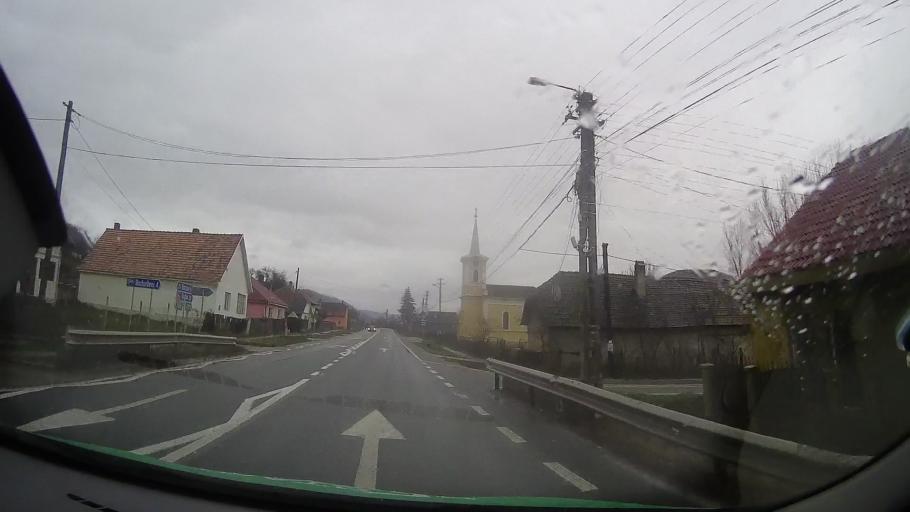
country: RO
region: Bistrita-Nasaud
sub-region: Comuna Galatii Bistritei
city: Galatii Bistritei
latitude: 46.9478
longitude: 24.4549
